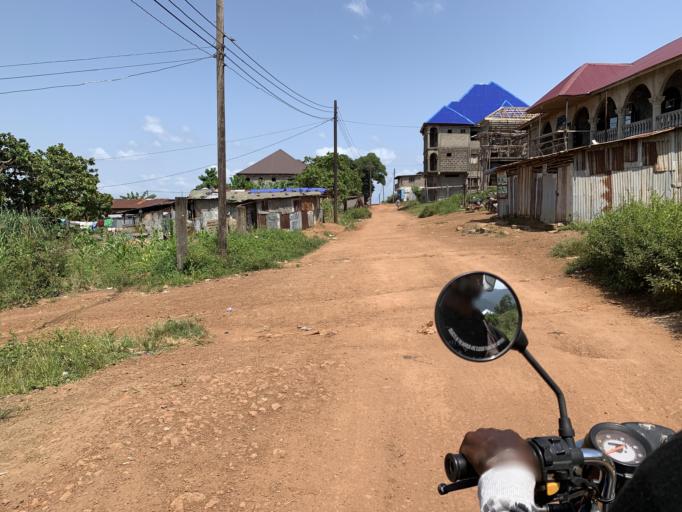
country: SL
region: Western Area
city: Hastings
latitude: 8.3807
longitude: -13.1465
